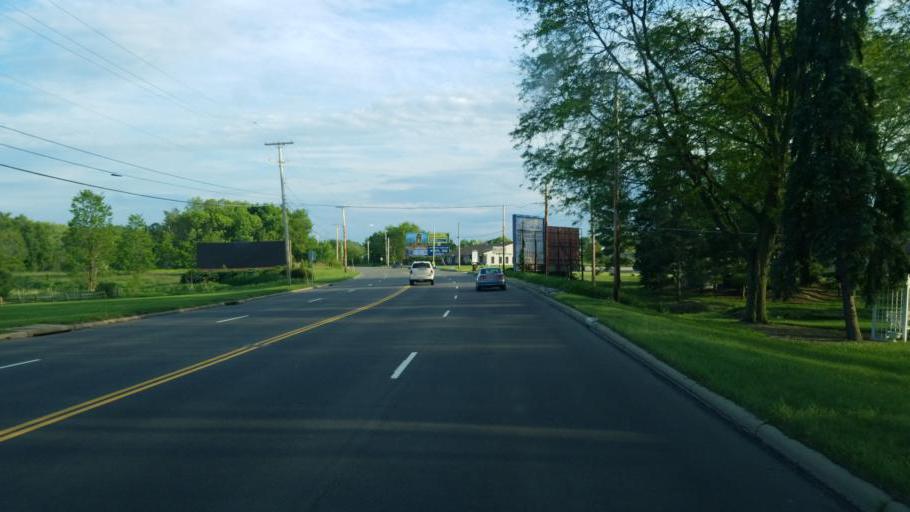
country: US
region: Ohio
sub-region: Stark County
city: Uniontown
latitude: 40.9624
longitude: -81.4092
